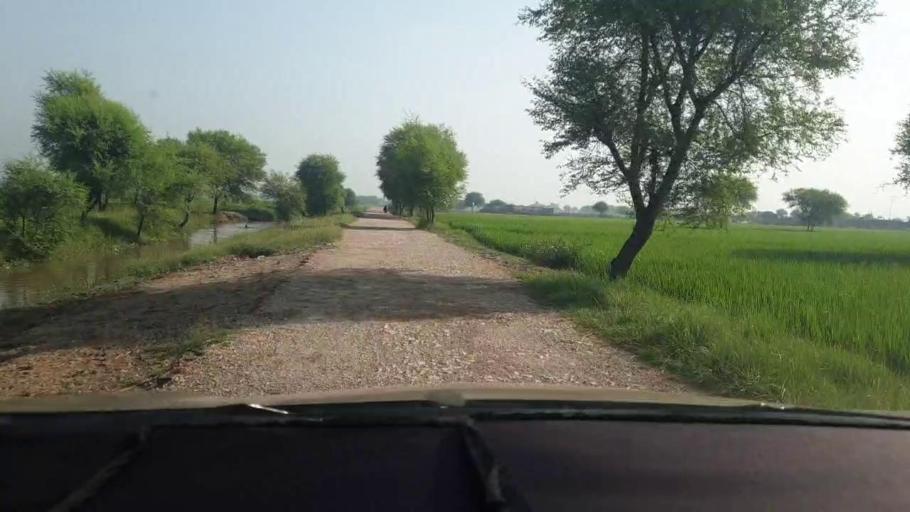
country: PK
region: Sindh
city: Kambar
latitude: 27.5917
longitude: 68.1062
